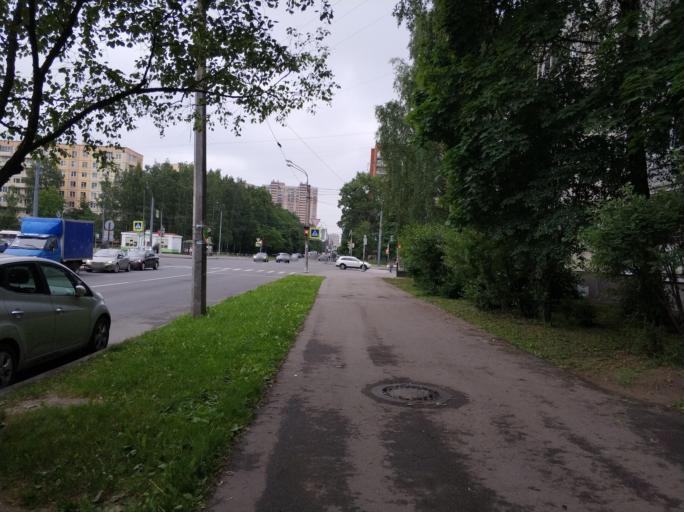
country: RU
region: St.-Petersburg
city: Grazhdanka
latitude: 60.0343
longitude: 30.3926
